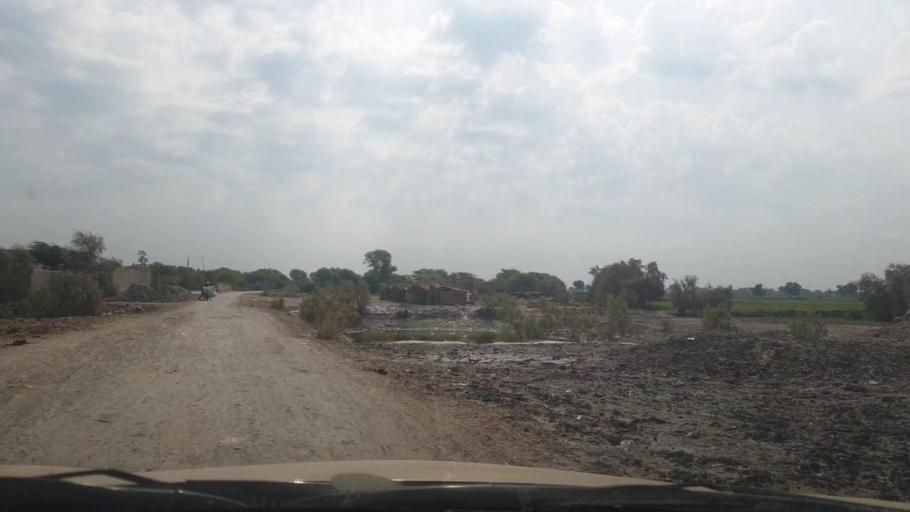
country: PK
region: Sindh
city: Larkana
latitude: 27.6521
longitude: 68.2030
